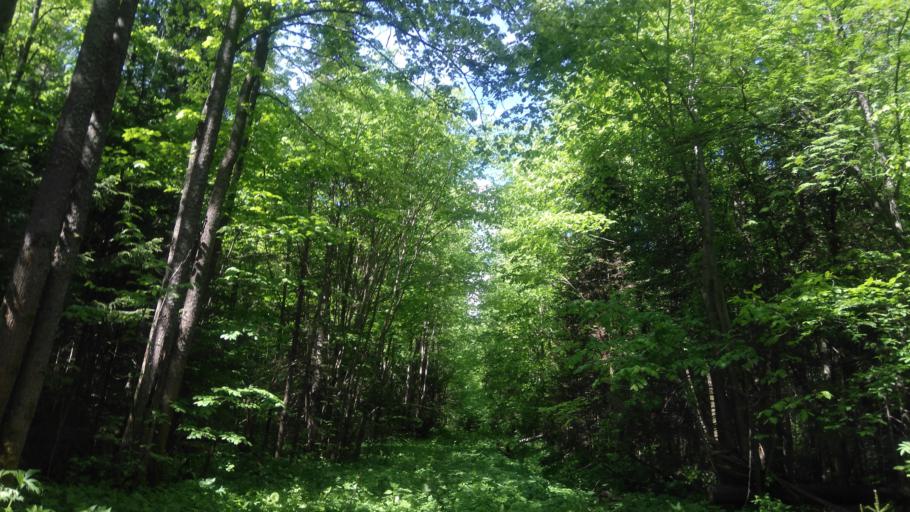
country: RU
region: Perm
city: Ferma
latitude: 57.9641
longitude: 56.3462
